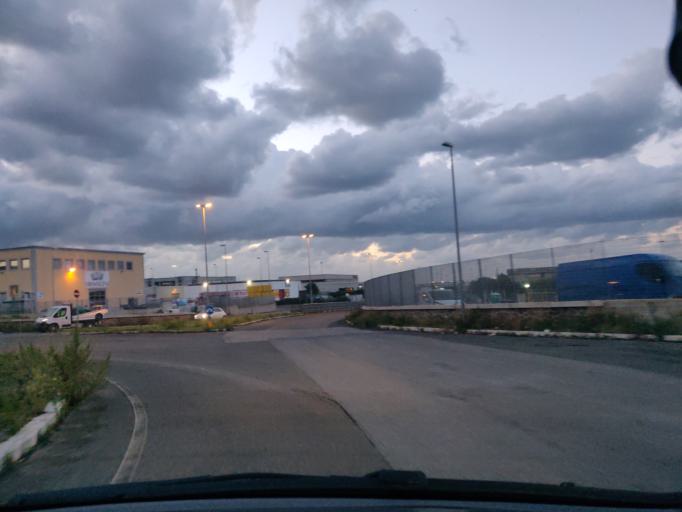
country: IT
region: Latium
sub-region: Citta metropolitana di Roma Capitale
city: Aurelia
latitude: 42.1245
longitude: 11.7776
